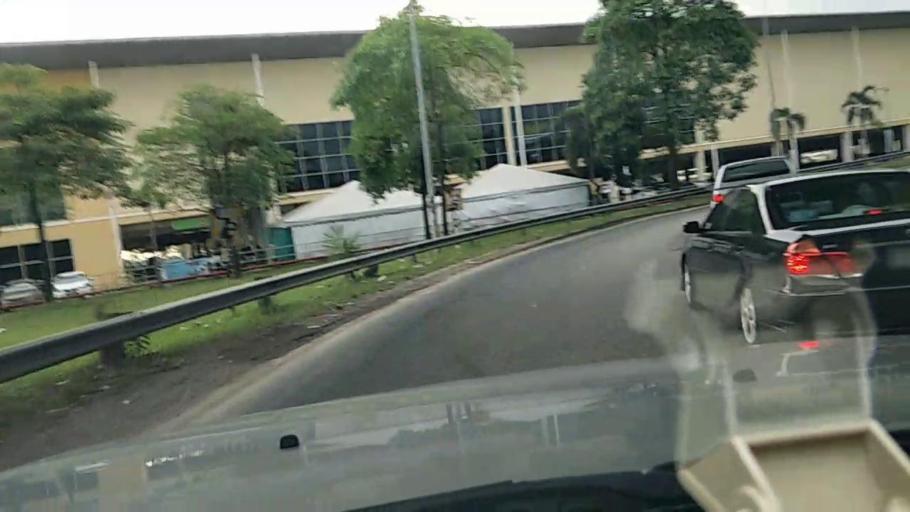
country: MY
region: Selangor
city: Klang
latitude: 3.1068
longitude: 101.4422
